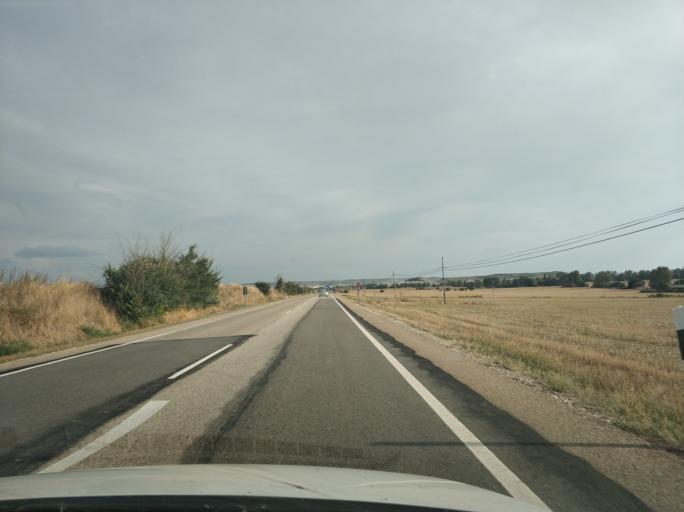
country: ES
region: Castille and Leon
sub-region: Provincia de Burgos
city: Quintanaortuno
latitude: 42.4820
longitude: -3.6940
